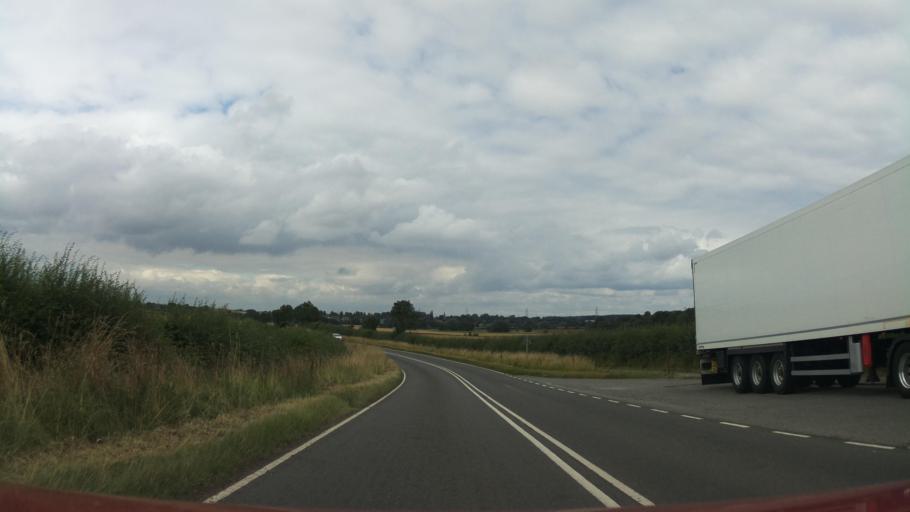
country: GB
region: England
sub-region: District of Rutland
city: Ryhall
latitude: 52.6688
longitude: -0.4685
